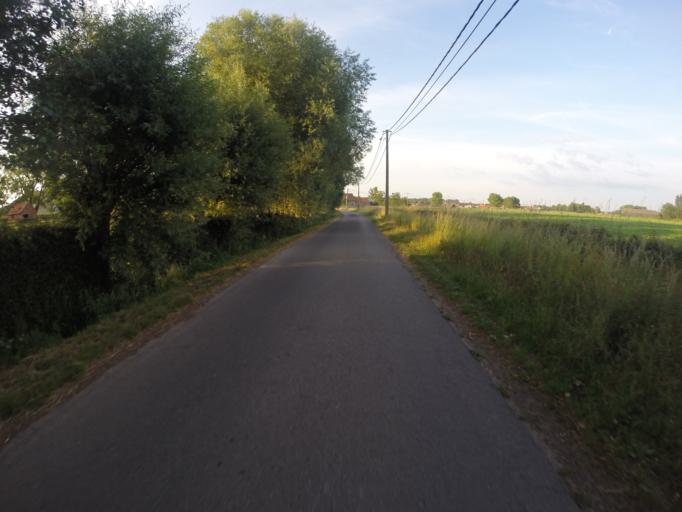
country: BE
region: Flanders
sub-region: Provincie West-Vlaanderen
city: Beernem
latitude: 51.1475
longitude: 3.2981
